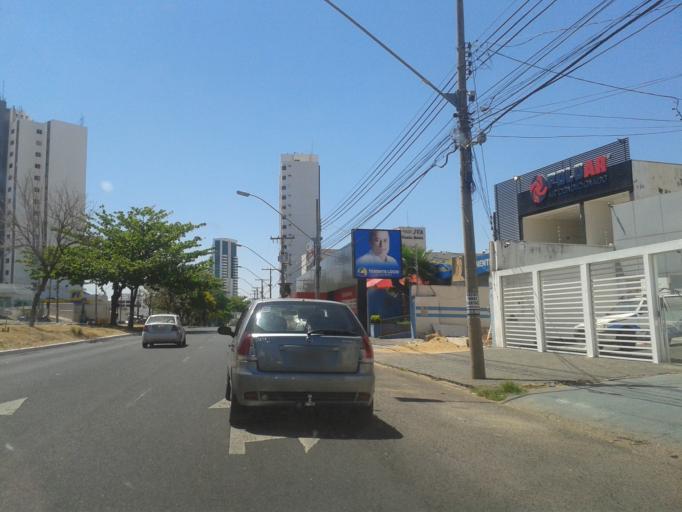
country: BR
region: Minas Gerais
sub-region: Uberlandia
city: Uberlandia
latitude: -18.9139
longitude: -48.2674
